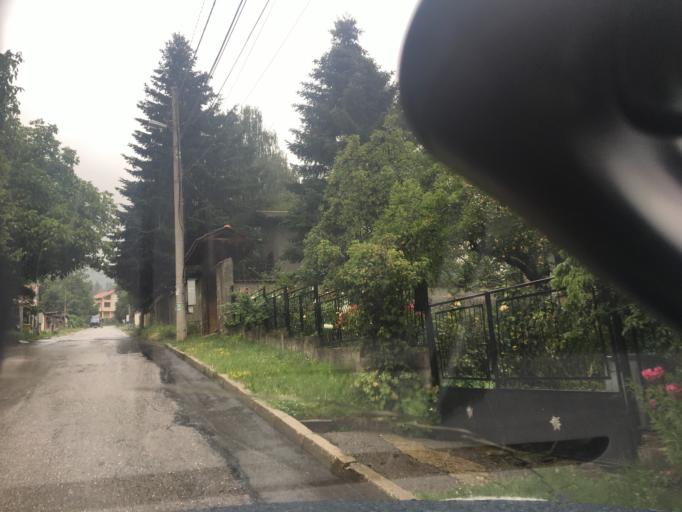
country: BG
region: Sofia-Capital
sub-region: Stolichna Obshtina
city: Sofia
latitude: 42.5855
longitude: 23.3513
